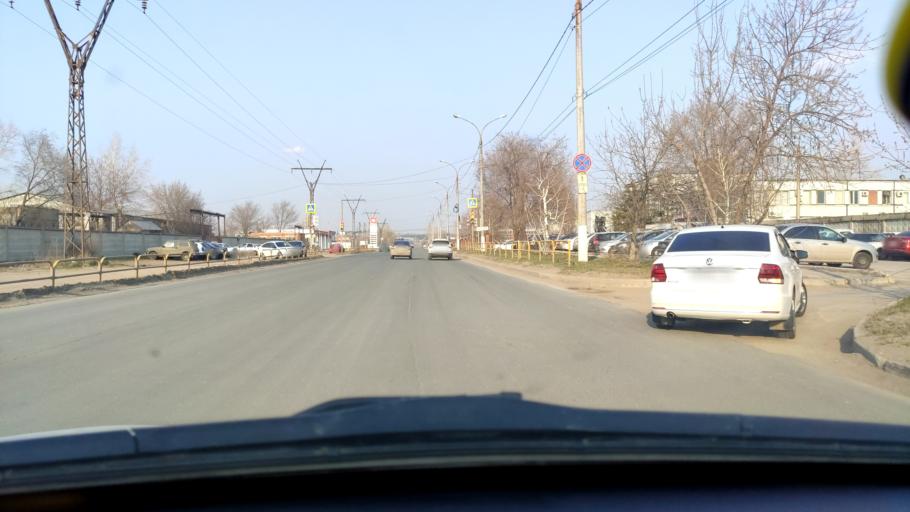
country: RU
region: Samara
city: Zhigulevsk
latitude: 53.4811
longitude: 49.4950
